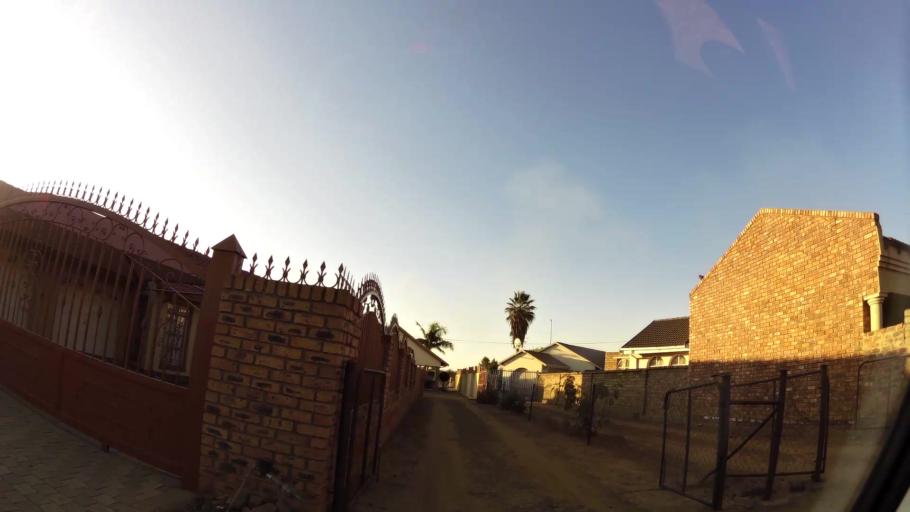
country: ZA
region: Gauteng
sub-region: City of Tshwane Metropolitan Municipality
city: Cullinan
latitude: -25.7232
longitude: 28.3916
